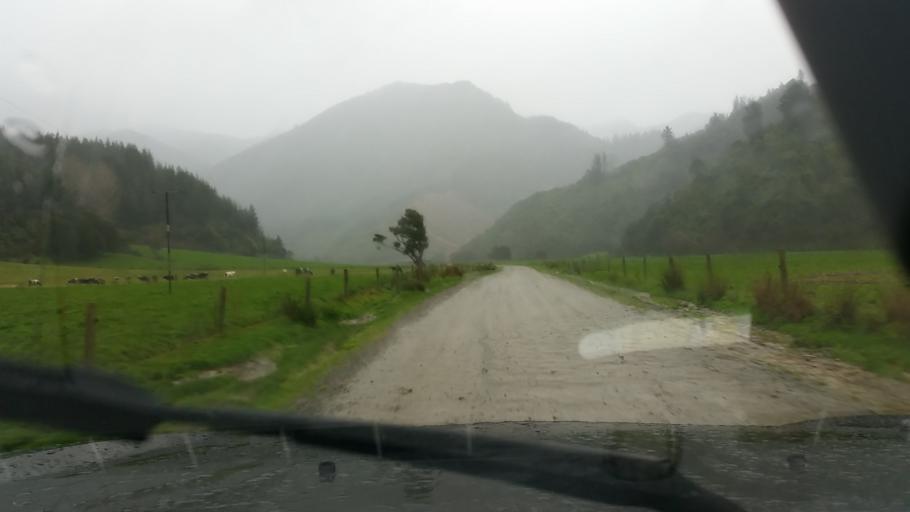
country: NZ
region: Marlborough
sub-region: Marlborough District
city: Picton
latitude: -41.3559
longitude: 173.9279
